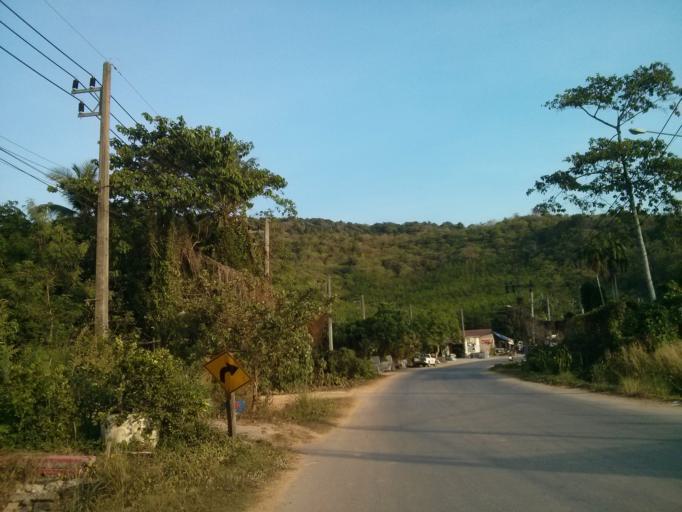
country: TH
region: Krabi
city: Saladan
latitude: 7.5665
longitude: 99.0405
